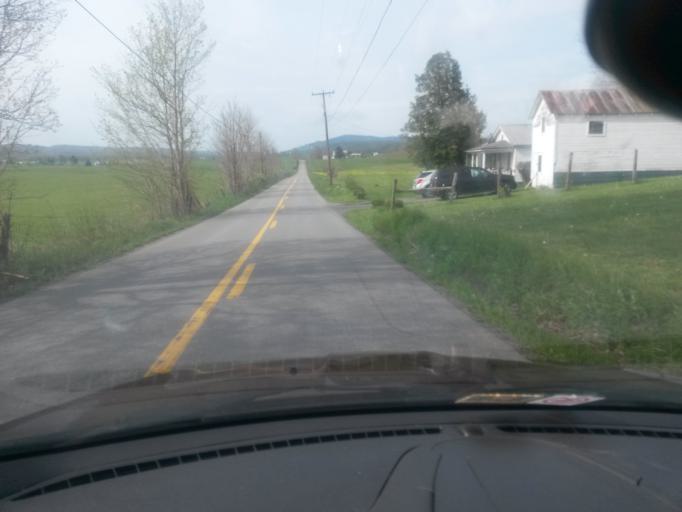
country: US
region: West Virginia
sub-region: Pocahontas County
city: Marlinton
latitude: 38.1311
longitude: -80.2105
